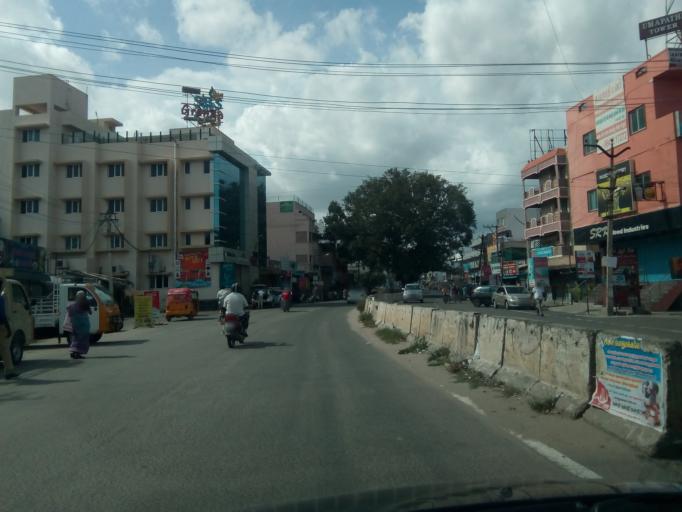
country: IN
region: Tamil Nadu
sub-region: Coimbatore
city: Singanallur
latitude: 11.0231
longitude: 77.0177
